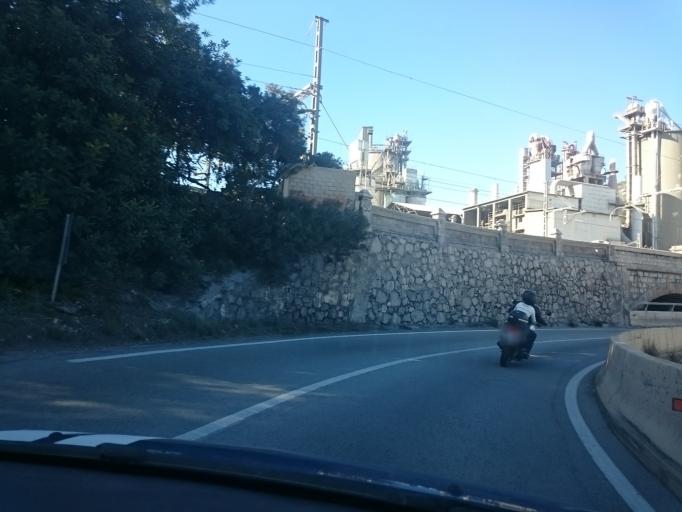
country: ES
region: Catalonia
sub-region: Provincia de Barcelona
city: Sitges
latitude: 41.2398
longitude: 1.8604
